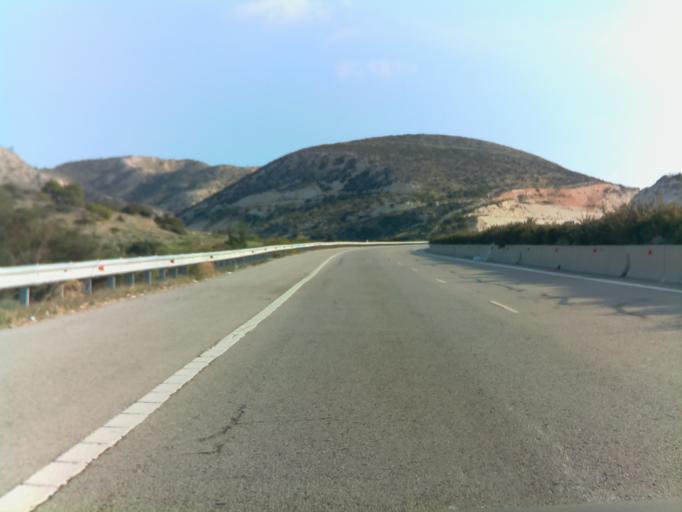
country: CY
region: Limassol
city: Pissouri
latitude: 34.6707
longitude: 32.6260
